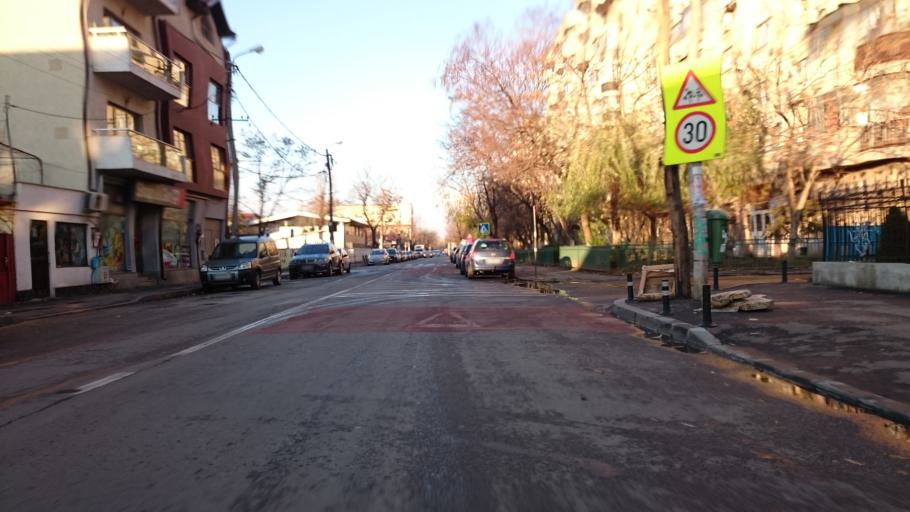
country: RO
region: Bucuresti
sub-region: Municipiul Bucuresti
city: Bucuresti
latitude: 44.4045
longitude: 26.0575
